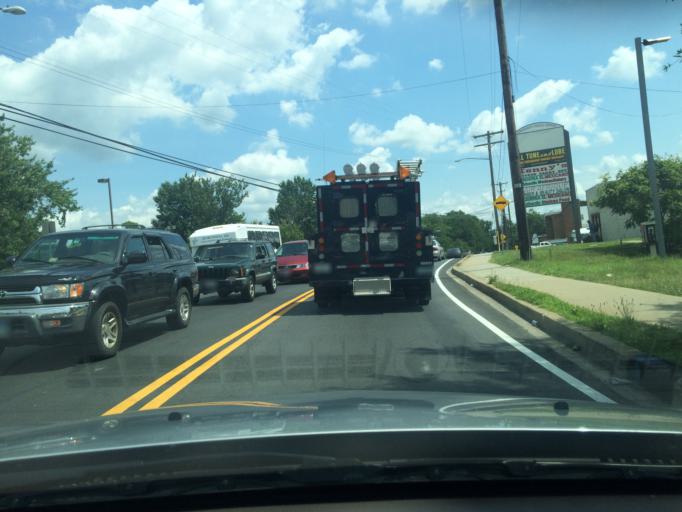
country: US
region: Maryland
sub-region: Prince George's County
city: Langley Park
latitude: 38.9843
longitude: -76.9791
